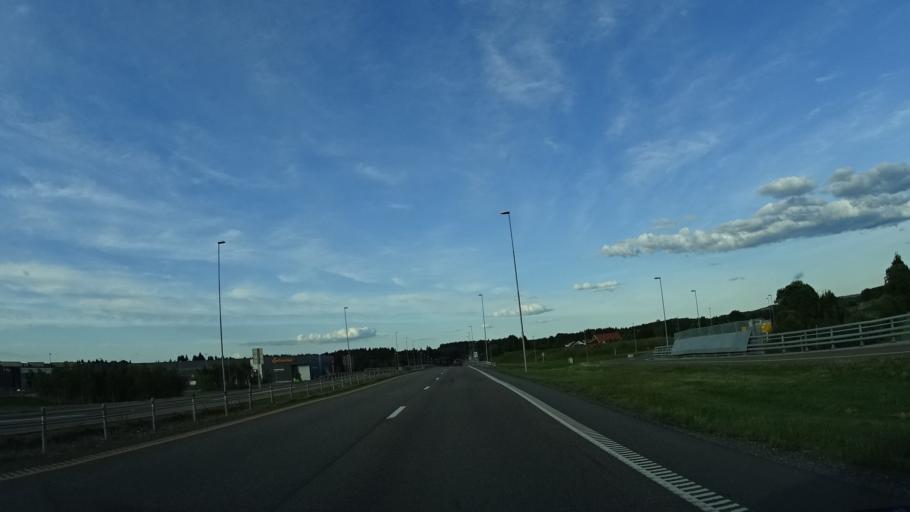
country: NO
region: Ostfold
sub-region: Askim
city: Askim
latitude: 59.5730
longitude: 11.2168
